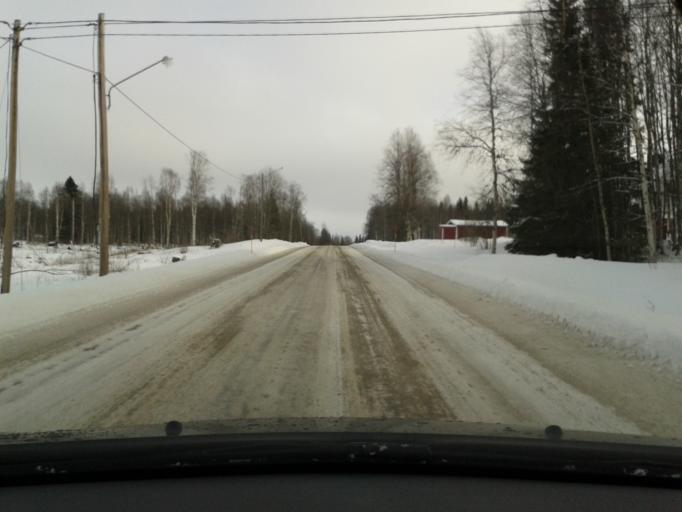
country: SE
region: Vaesterbotten
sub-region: Vilhelmina Kommun
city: Sjoberg
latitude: 64.7933
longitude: 16.0812
